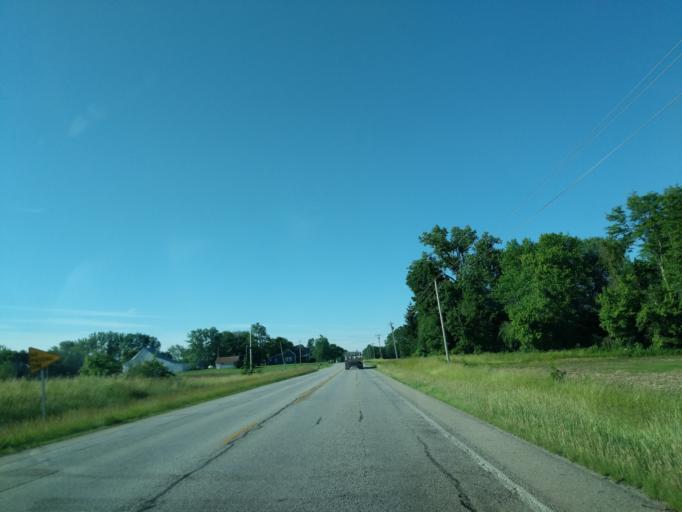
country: US
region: Indiana
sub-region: Shelby County
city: Morristown
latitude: 39.6575
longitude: -85.7729
